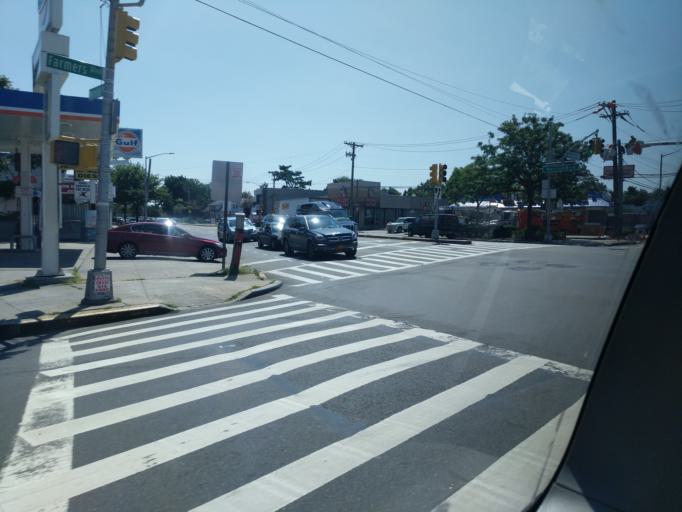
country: US
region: New York
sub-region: Queens County
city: Jamaica
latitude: 40.6799
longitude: -73.7616
